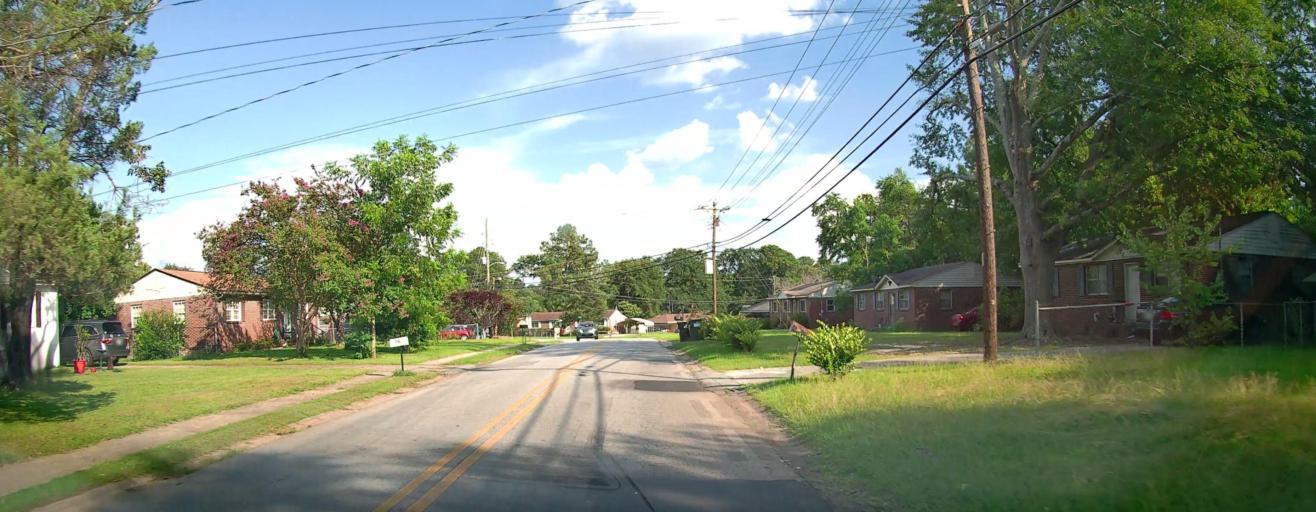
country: US
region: Georgia
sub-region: Houston County
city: Centerville
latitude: 32.6000
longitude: -83.6530
